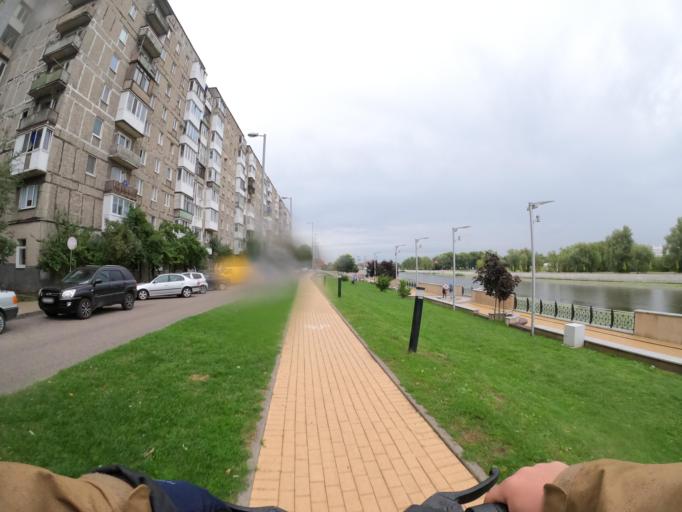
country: RU
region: Kaliningrad
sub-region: Gorod Kaliningrad
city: Kaliningrad
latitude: 54.7075
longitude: 20.5279
